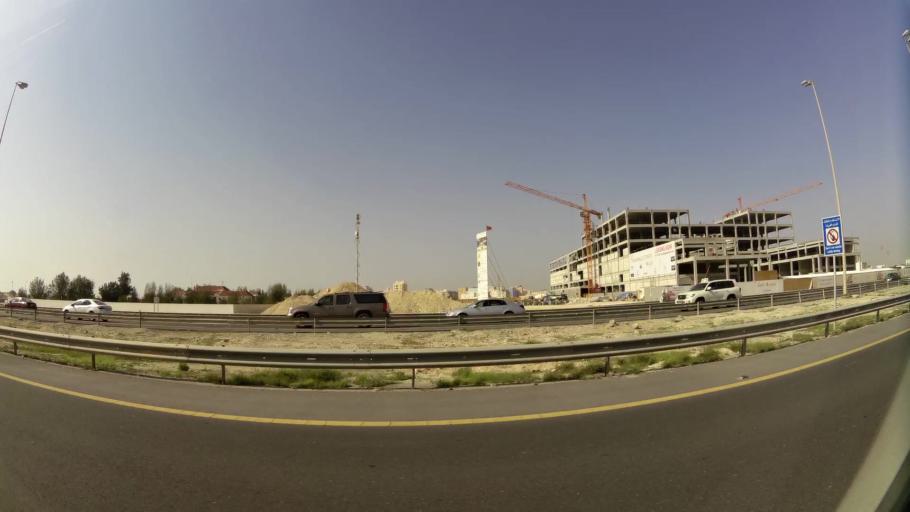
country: BH
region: Central Governorate
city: Madinat Hamad
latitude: 26.1746
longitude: 50.4834
